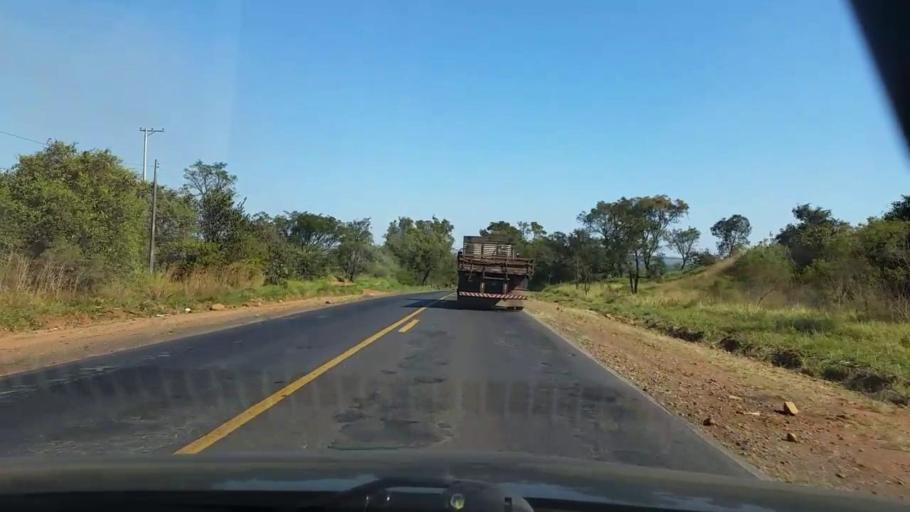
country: BR
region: Sao Paulo
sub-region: Sao Manuel
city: Sao Manuel
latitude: -22.7915
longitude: -48.6549
